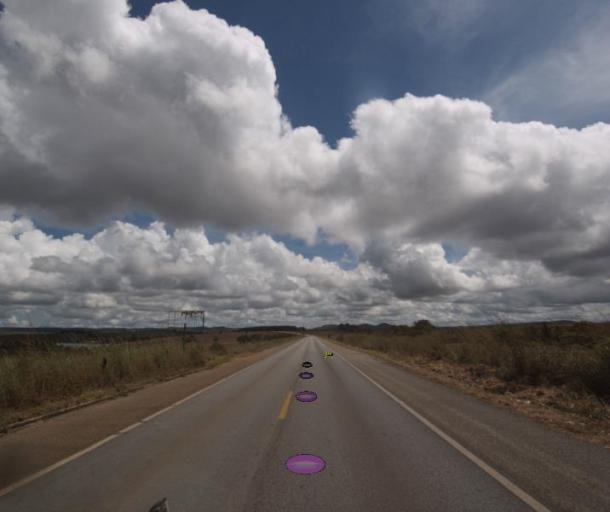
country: BR
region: Goias
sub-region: Pirenopolis
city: Pirenopolis
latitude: -15.7491
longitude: -48.6593
